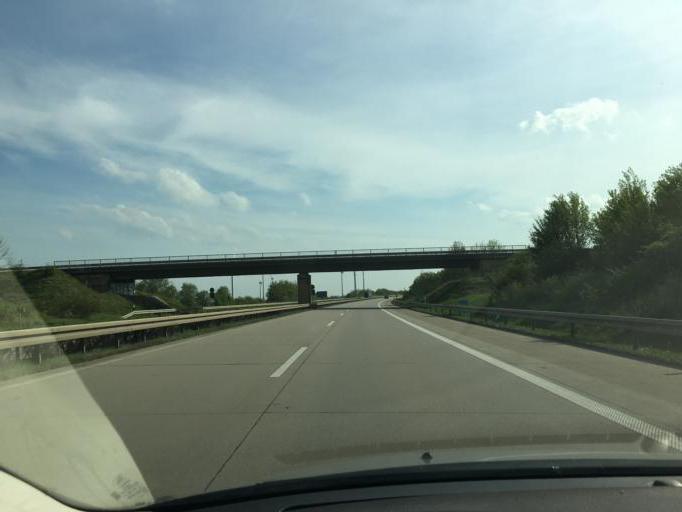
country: DE
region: Saxony-Anhalt
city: Dahlenwarsleben
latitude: 52.1912
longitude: 11.5514
